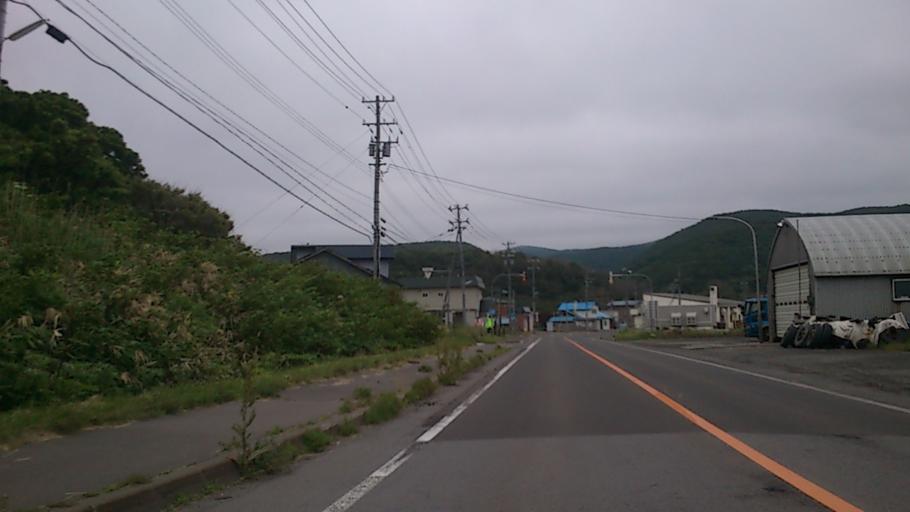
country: JP
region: Hokkaido
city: Iwanai
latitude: 42.7493
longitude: 140.1336
